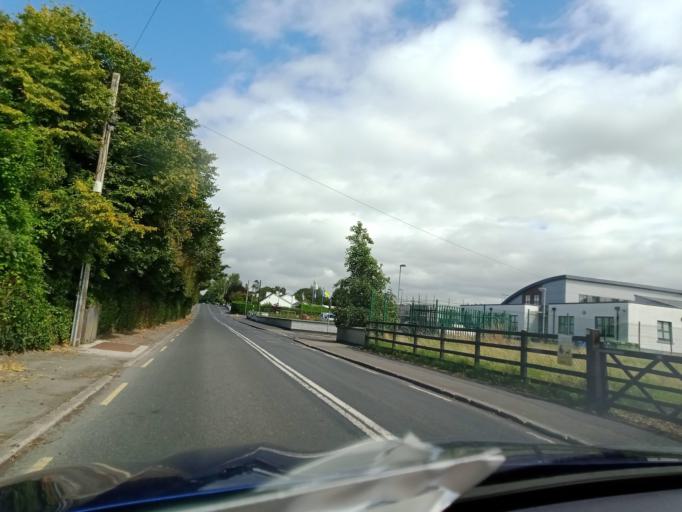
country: IE
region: Leinster
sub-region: Laois
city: Abbeyleix
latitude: 52.9183
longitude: -7.3443
